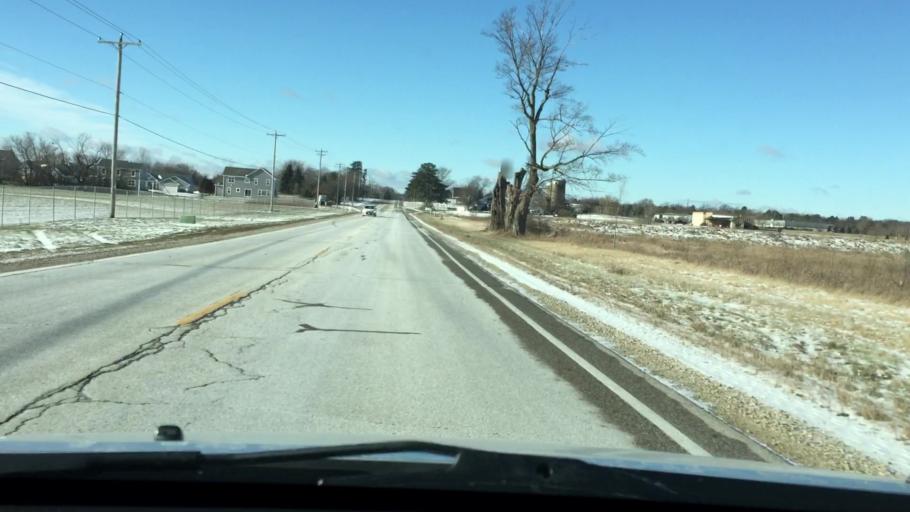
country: US
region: Wisconsin
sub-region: Waukesha County
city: Eagle
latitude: 42.8789
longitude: -88.4517
